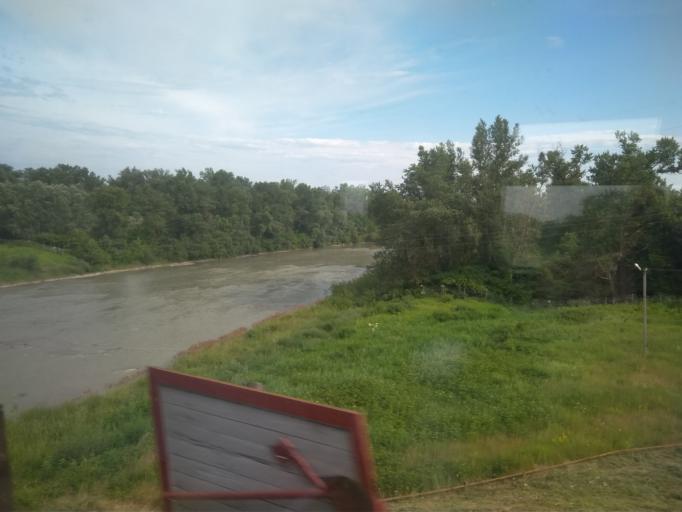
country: RU
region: Krasnodarskiy
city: Pshekhskaya
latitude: 44.7159
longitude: 39.8022
